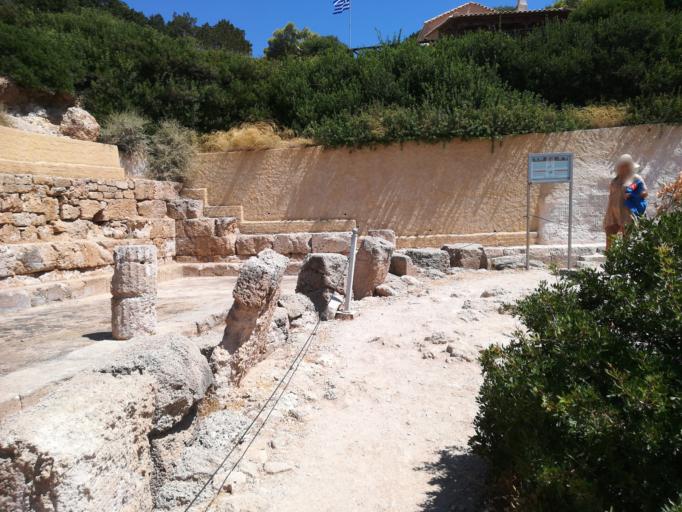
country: GR
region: Peloponnese
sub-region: Nomos Korinthias
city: Vrakhati
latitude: 38.0281
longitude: 22.8529
